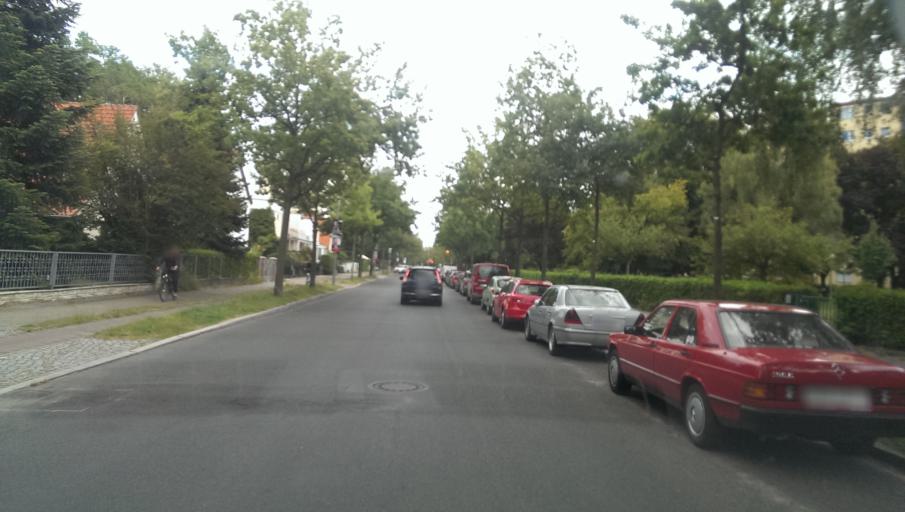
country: DE
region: Berlin
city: Zehlendorf Bezirk
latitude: 52.4205
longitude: 13.2471
